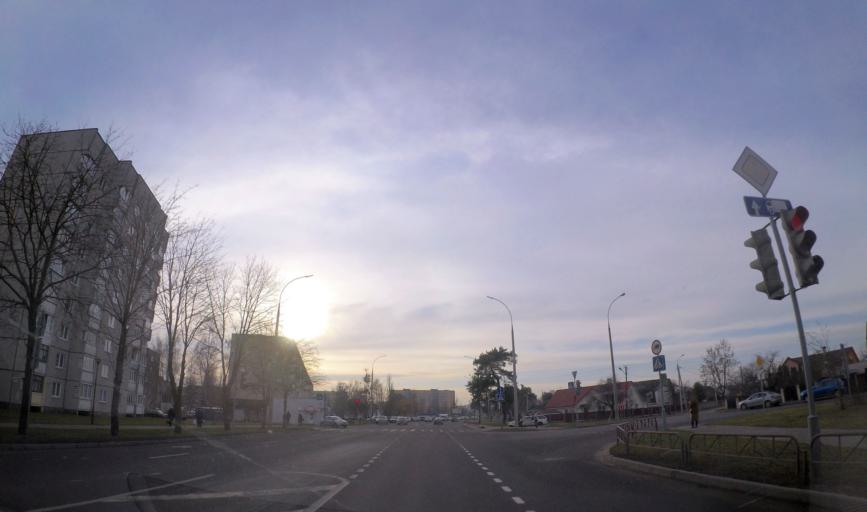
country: BY
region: Grodnenskaya
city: Hrodna
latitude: 53.6679
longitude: 23.7893
